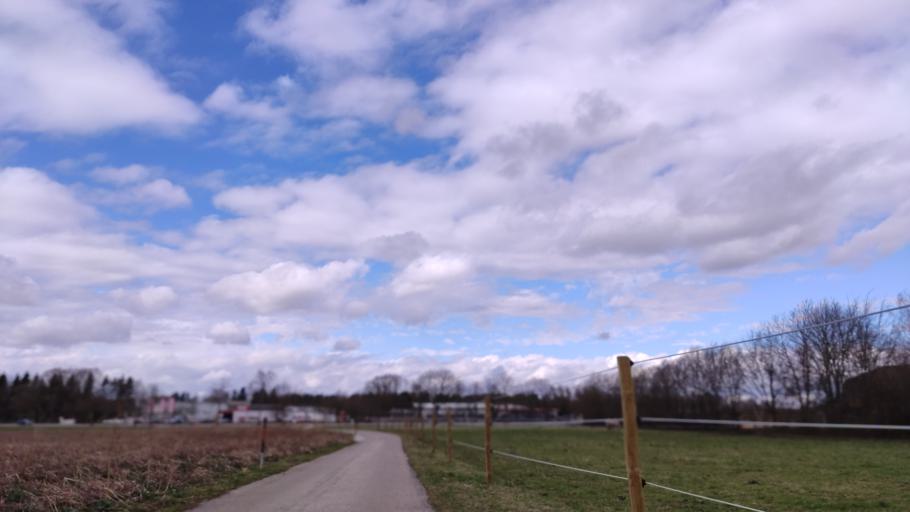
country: DE
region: Bavaria
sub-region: Upper Bavaria
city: Emmering
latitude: 48.1797
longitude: 11.2937
